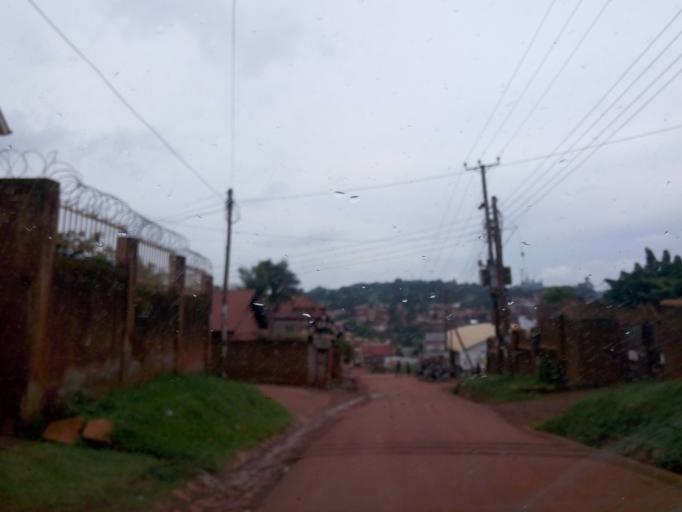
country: UG
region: Central Region
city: Kampala Central Division
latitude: 0.3319
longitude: 32.5629
